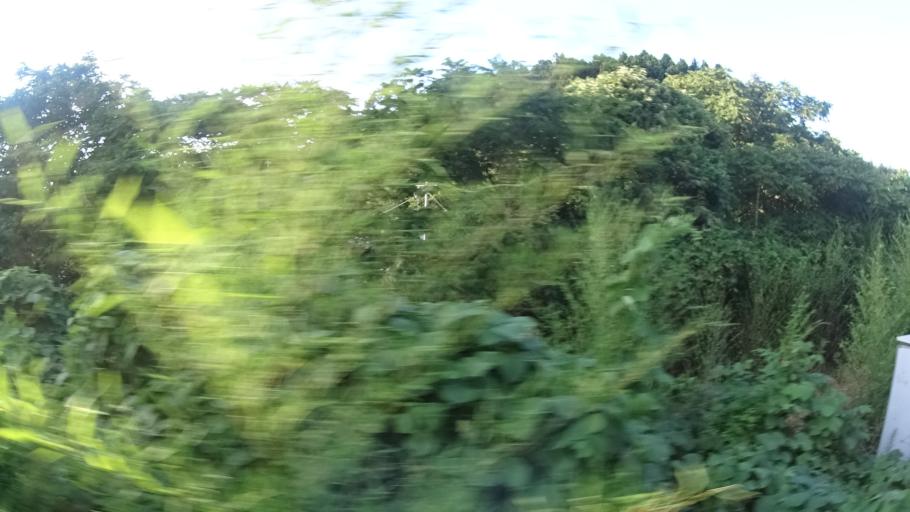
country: JP
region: Fukushima
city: Koriyama
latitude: 37.4168
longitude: 140.4319
